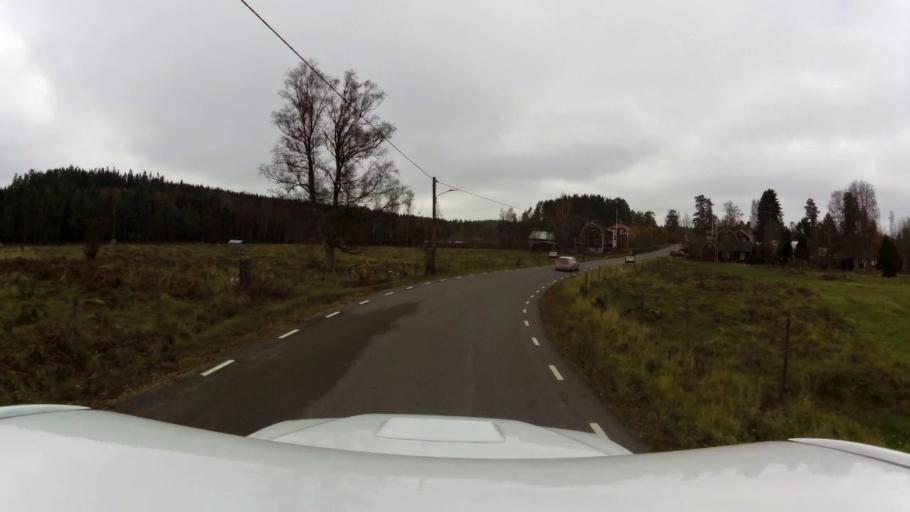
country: SE
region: OEstergoetland
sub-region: Kinda Kommun
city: Kisa
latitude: 58.1215
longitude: 15.4258
